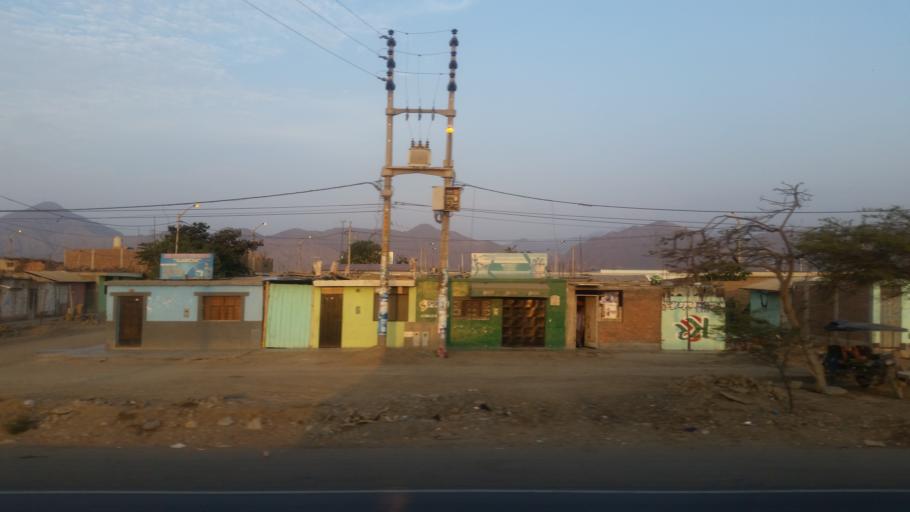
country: PE
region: La Libertad
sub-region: Ascope
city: Chicama
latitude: -7.8703
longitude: -79.1350
